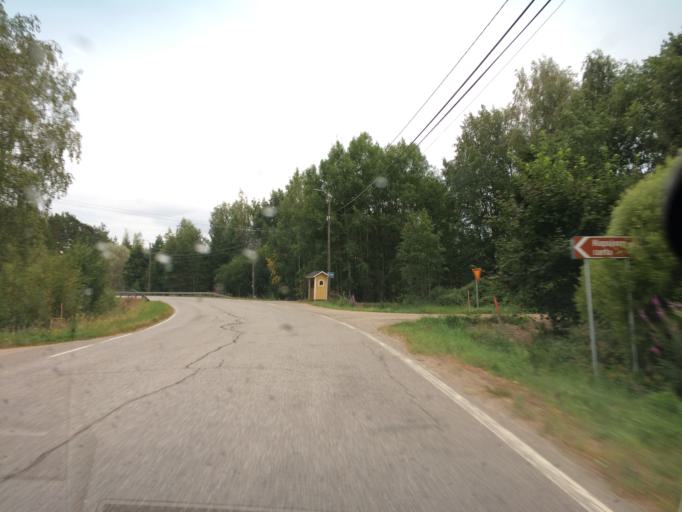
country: FI
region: Haeme
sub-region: Haemeenlinna
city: Tuulos
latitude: 61.1760
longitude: 24.7601
